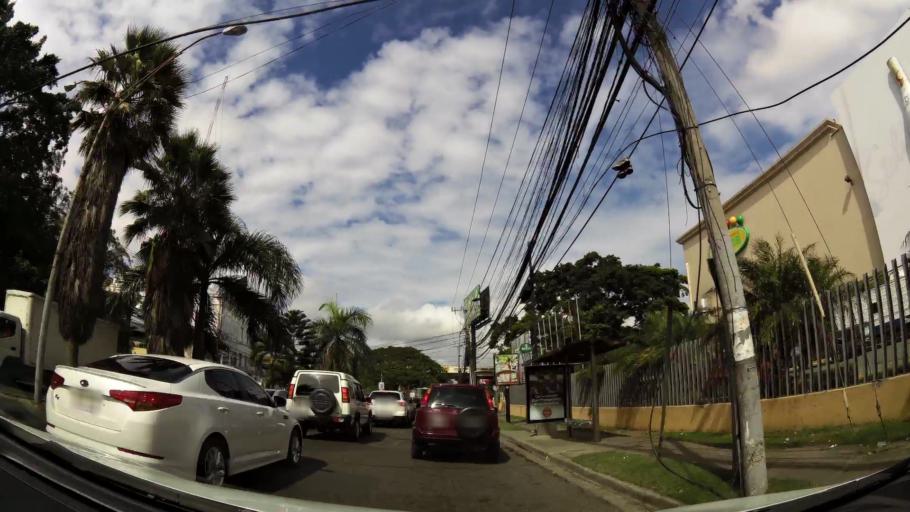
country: DO
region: Santiago
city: Santiago de los Caballeros
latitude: 19.4608
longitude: -70.6849
